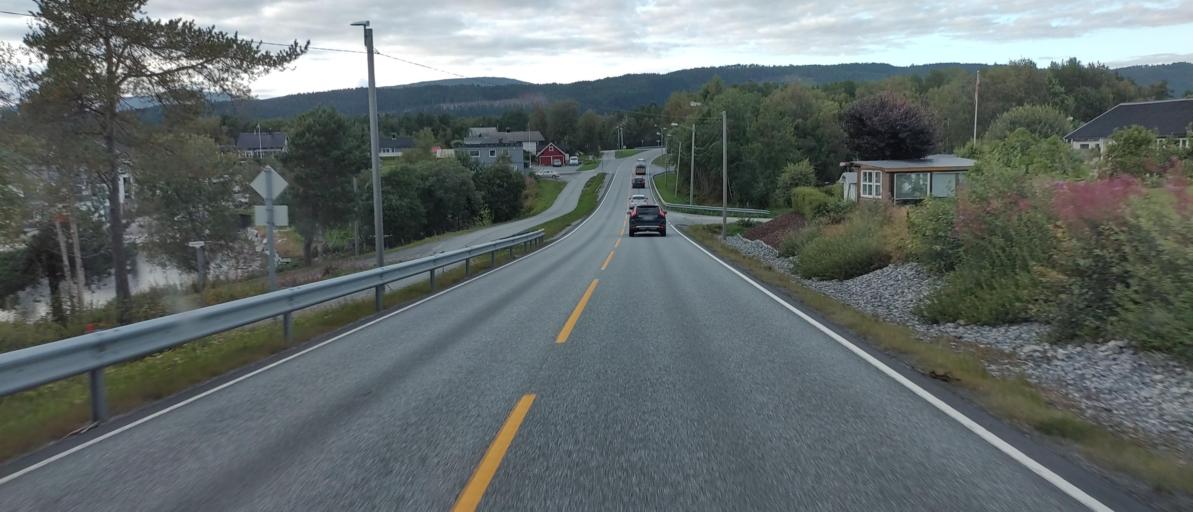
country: NO
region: More og Romsdal
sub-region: Molde
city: Hjelset
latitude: 62.7162
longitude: 7.4279
